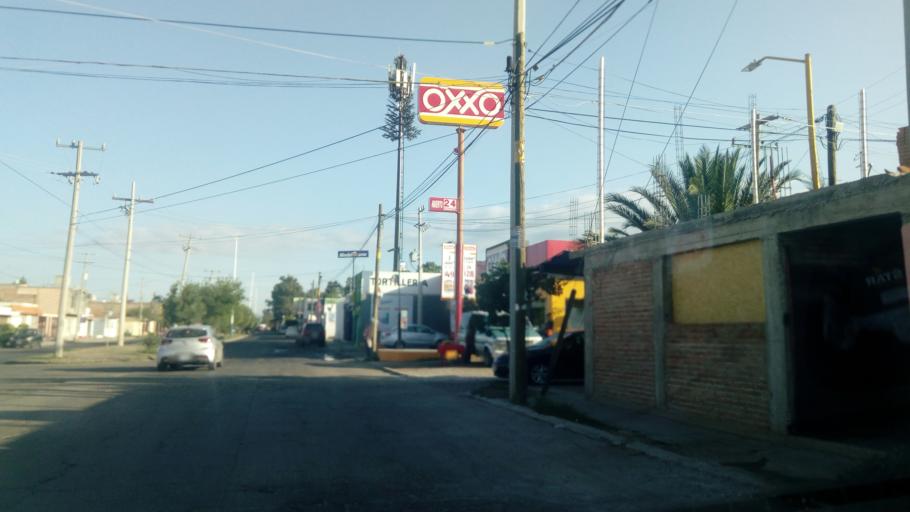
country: MX
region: Durango
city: Victoria de Durango
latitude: 24.0441
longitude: -104.6128
